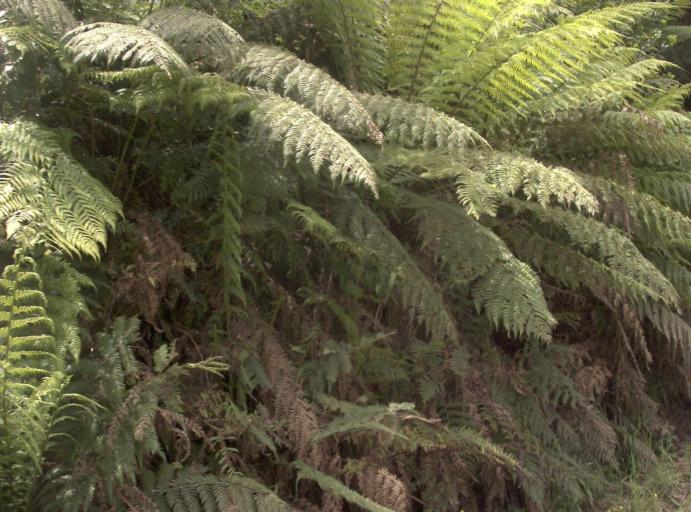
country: AU
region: Victoria
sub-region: Latrobe
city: Traralgon
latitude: -38.4233
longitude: 146.5685
